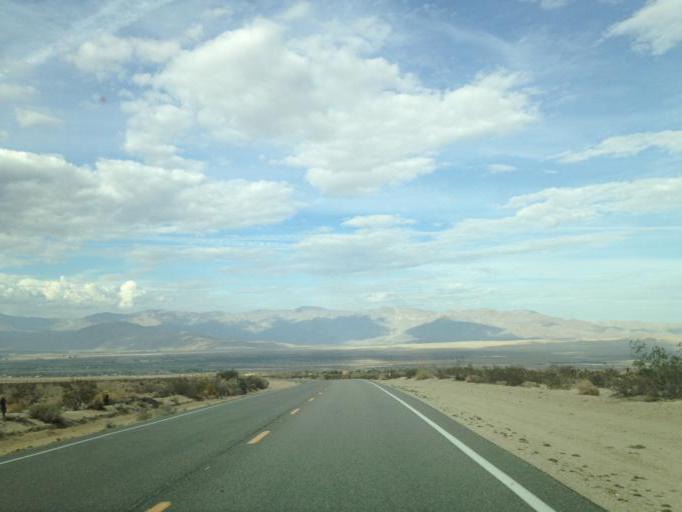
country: US
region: California
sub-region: San Diego County
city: Borrego Springs
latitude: 33.1750
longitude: -116.3338
